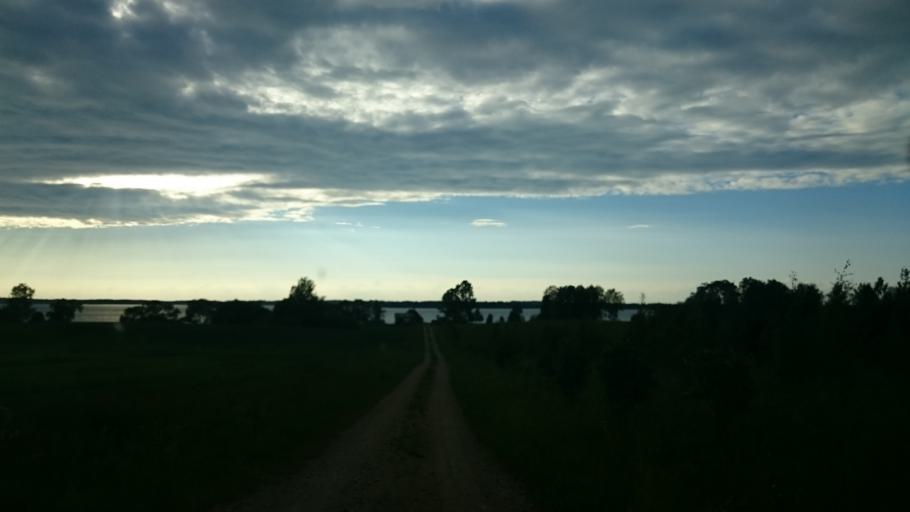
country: LV
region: Ludzas Rajons
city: Ludza
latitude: 56.5497
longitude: 27.6480
